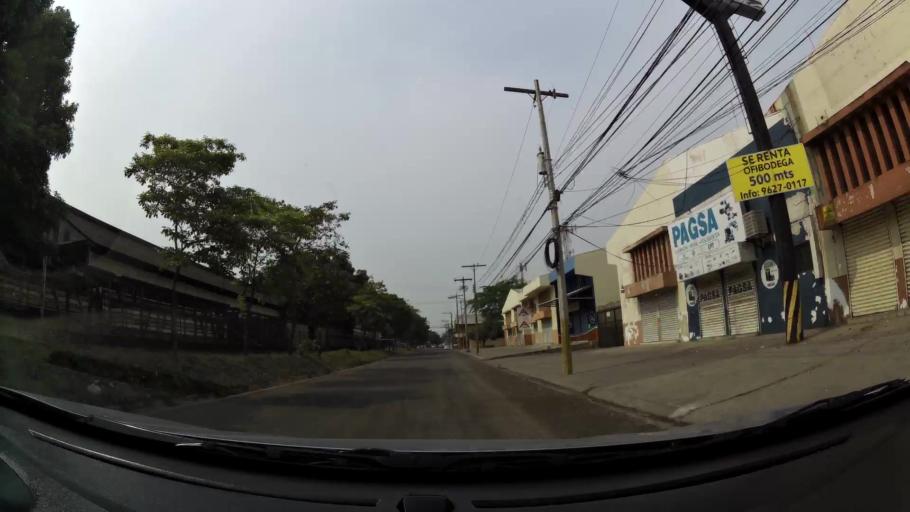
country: HN
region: Cortes
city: San Pedro Sula
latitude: 15.4967
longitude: -88.0242
